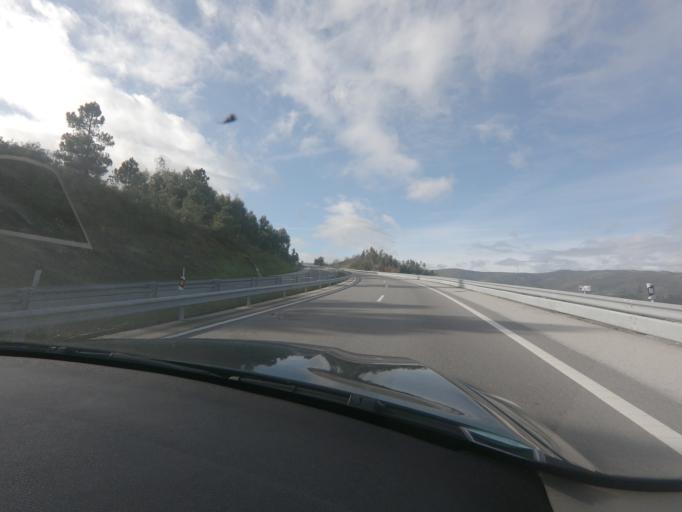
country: PT
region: Viseu
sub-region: Lamego
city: Lamego
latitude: 41.0742
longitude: -7.8148
